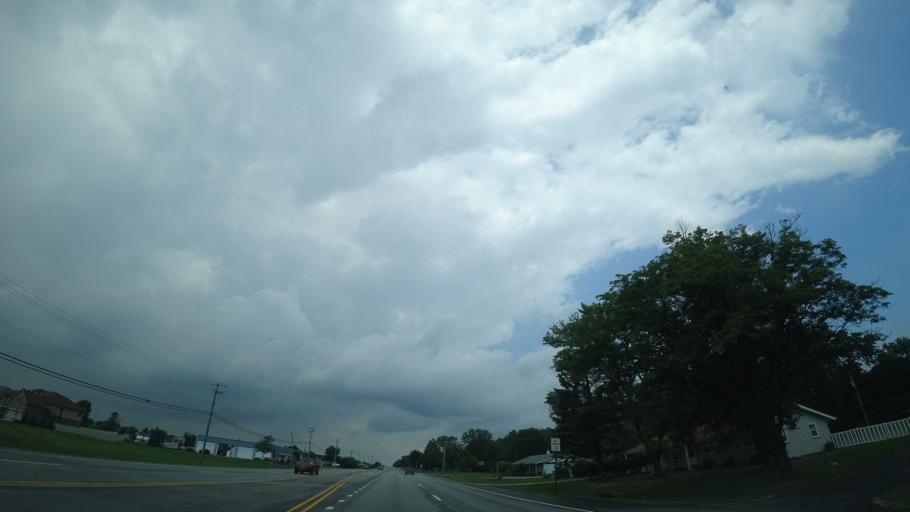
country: US
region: Illinois
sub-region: Cook County
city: Country Club Hills
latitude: 41.5476
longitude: -87.7327
